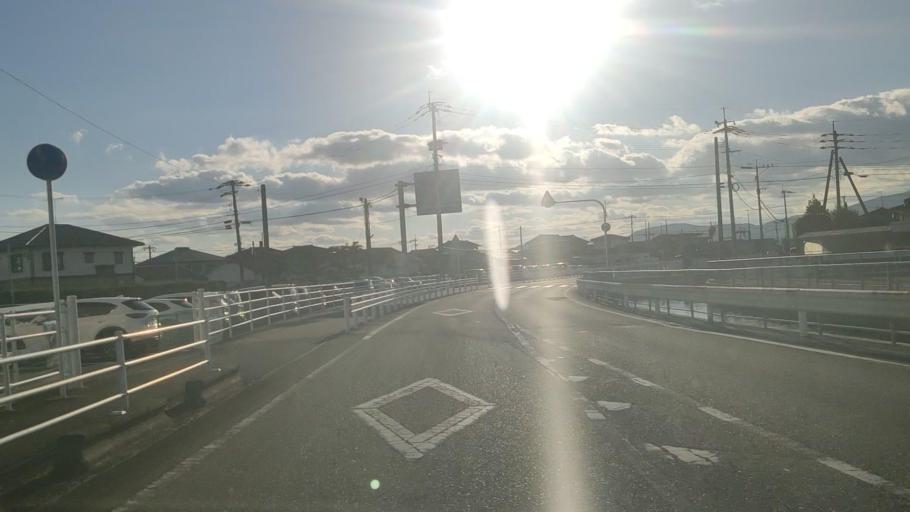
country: JP
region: Saga Prefecture
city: Saga-shi
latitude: 33.2736
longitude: 130.2208
